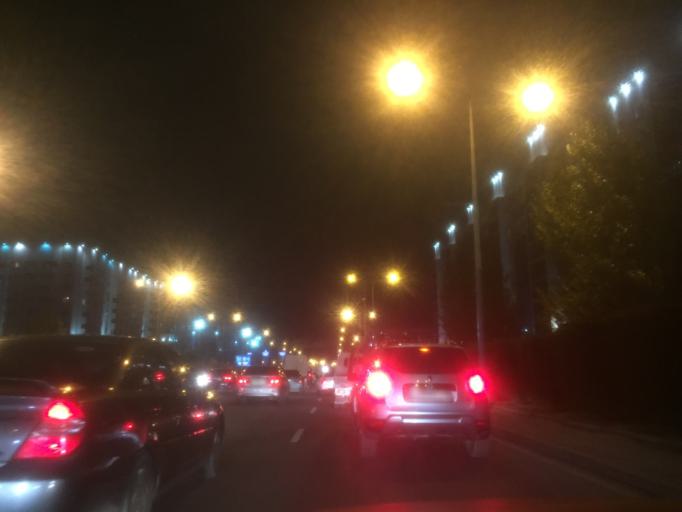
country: KZ
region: Astana Qalasy
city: Astana
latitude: 51.1345
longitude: 71.4273
